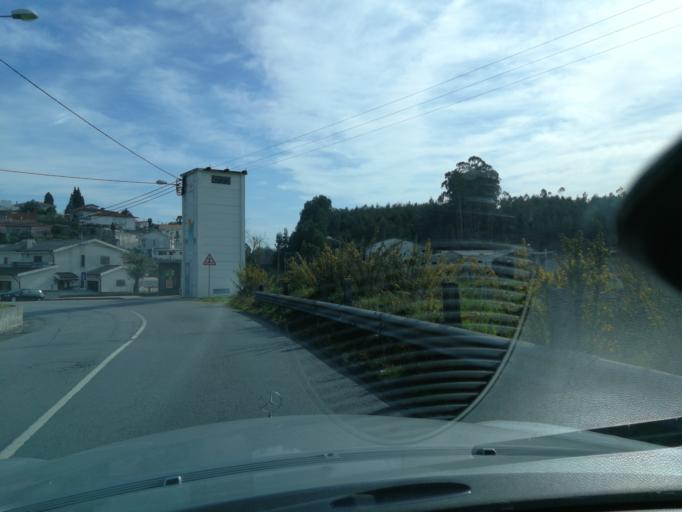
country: PT
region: Braga
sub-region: Vila Nova de Famalicao
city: Vila Nova de Famalicao
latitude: 41.4287
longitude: -8.5217
